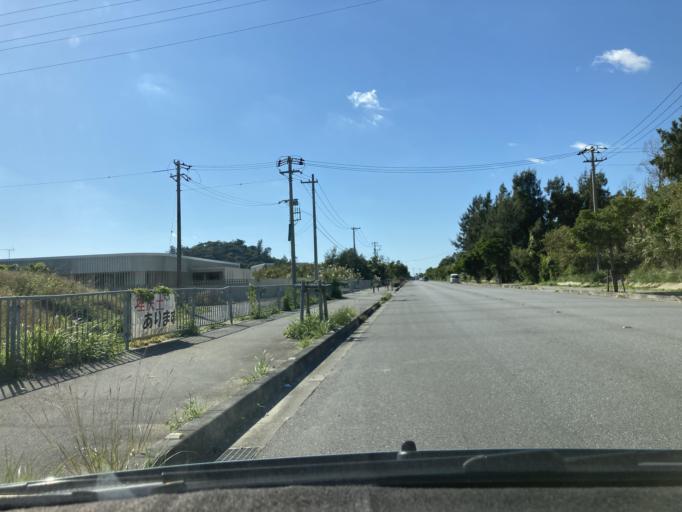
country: JP
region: Okinawa
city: Gushikawa
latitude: 26.3799
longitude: 127.8362
